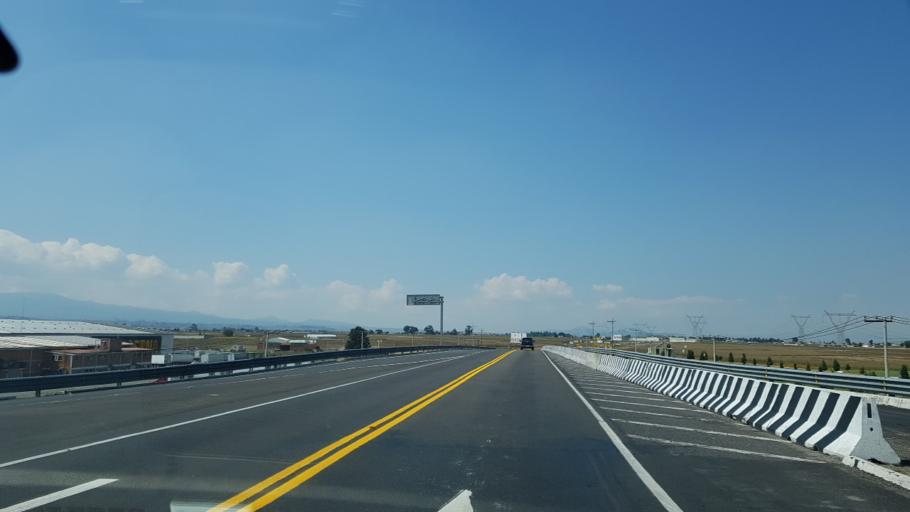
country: MX
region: Mexico
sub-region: Toluca
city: Sebastian Lerdo de Tejada
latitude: 19.3868
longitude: -99.7089
